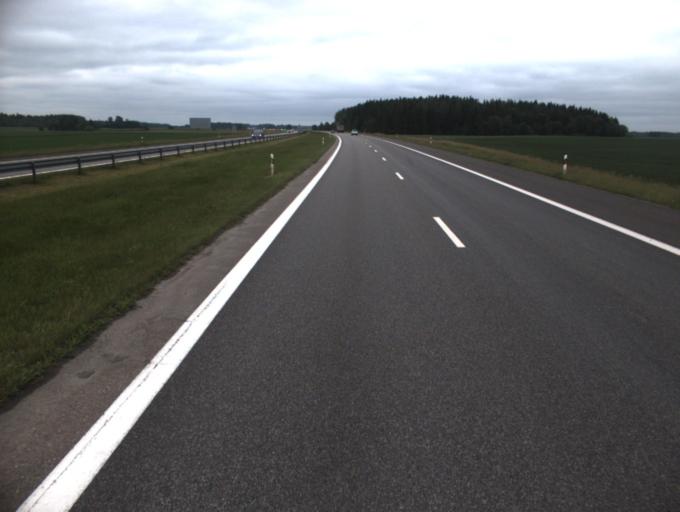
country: LT
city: Ariogala
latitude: 55.2852
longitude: 23.3042
